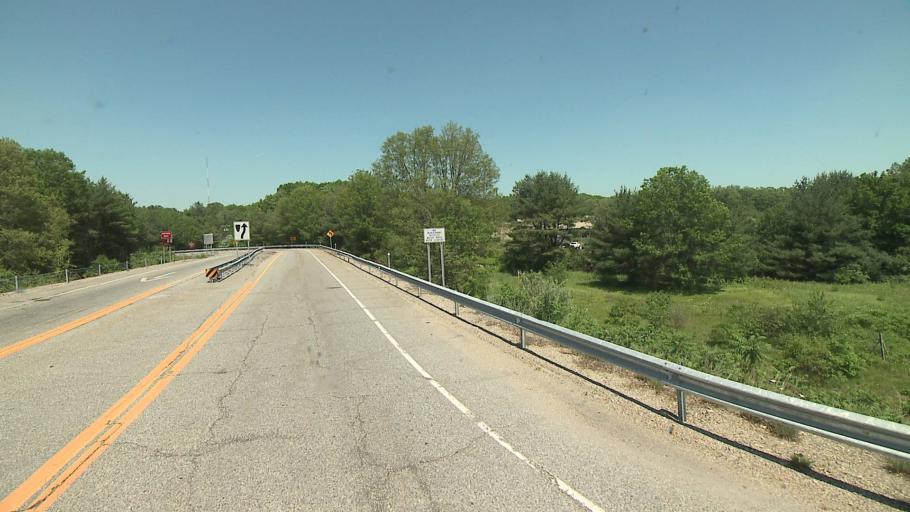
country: US
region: Connecticut
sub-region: Windham County
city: Putnam
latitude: 41.8987
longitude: -71.8974
